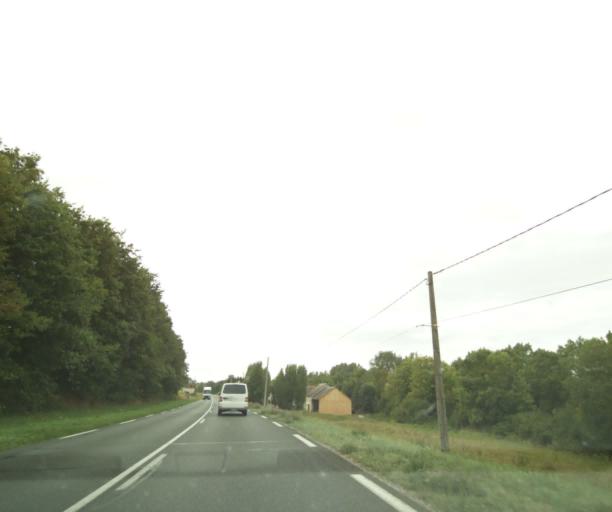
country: FR
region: Centre
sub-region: Departement d'Indre-et-Loire
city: Perrusson
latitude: 47.0701
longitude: 1.0765
